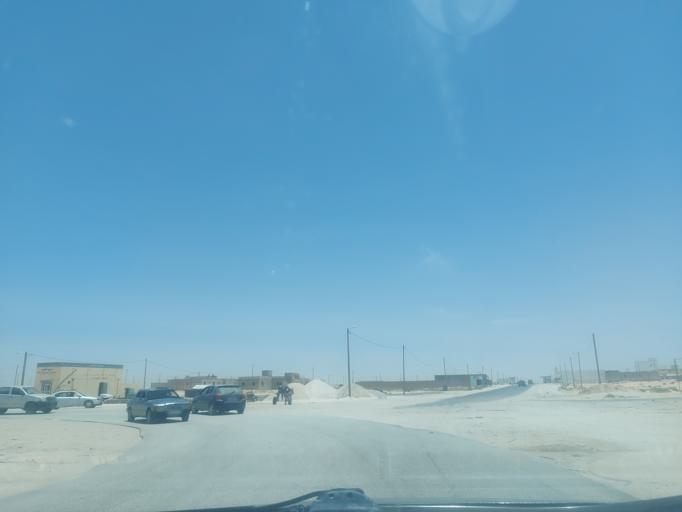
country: MR
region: Nouakchott
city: Nouakchott
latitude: 18.0859
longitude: -15.9518
